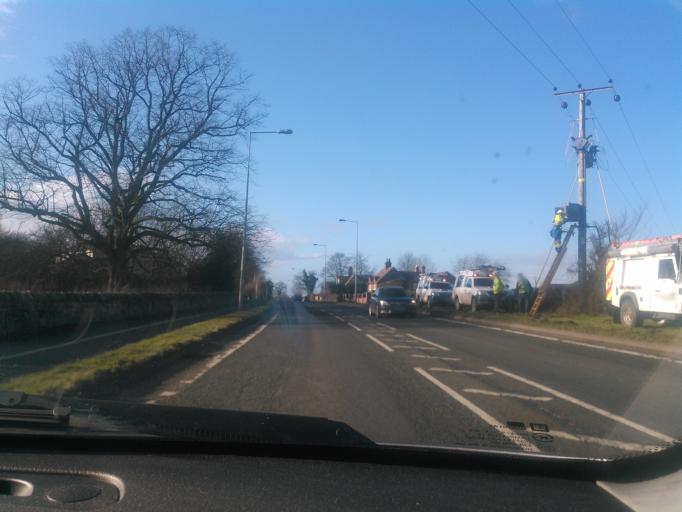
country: GB
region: England
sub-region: Telford and Wrekin
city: Eyton upon the Weald Moors
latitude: 52.7191
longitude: -2.5058
